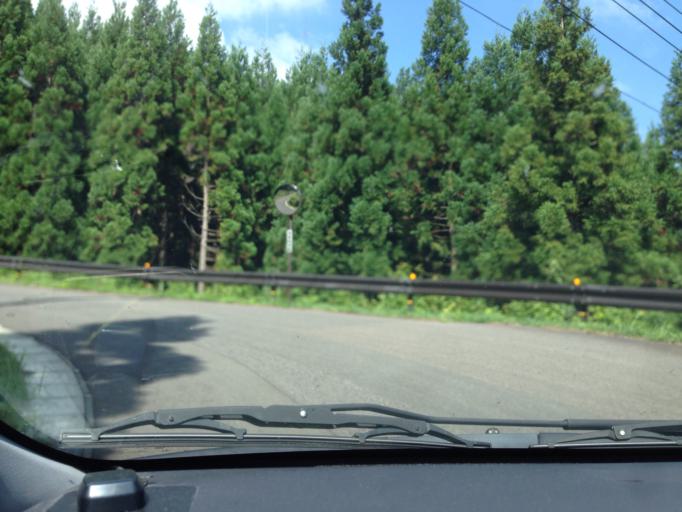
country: JP
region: Fukushima
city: Inawashiro
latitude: 37.3478
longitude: 140.0576
